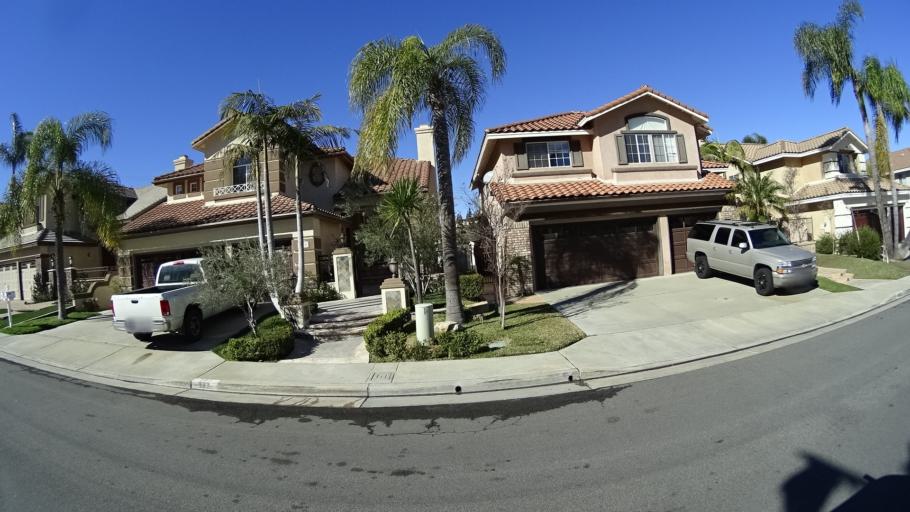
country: US
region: California
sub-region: Orange County
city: Yorba Linda
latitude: 33.8534
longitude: -117.7517
